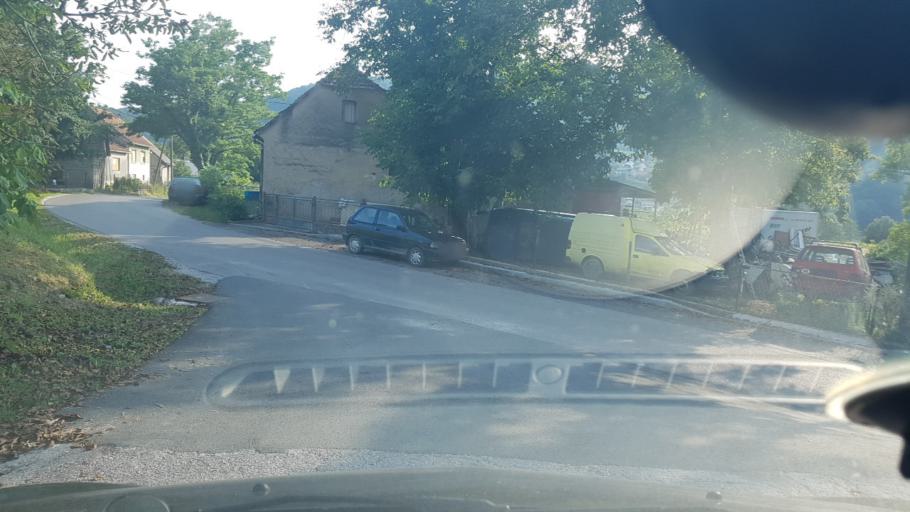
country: HR
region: Krapinsko-Zagorska
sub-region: Grad Krapina
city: Krapina
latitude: 46.1763
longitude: 15.8692
